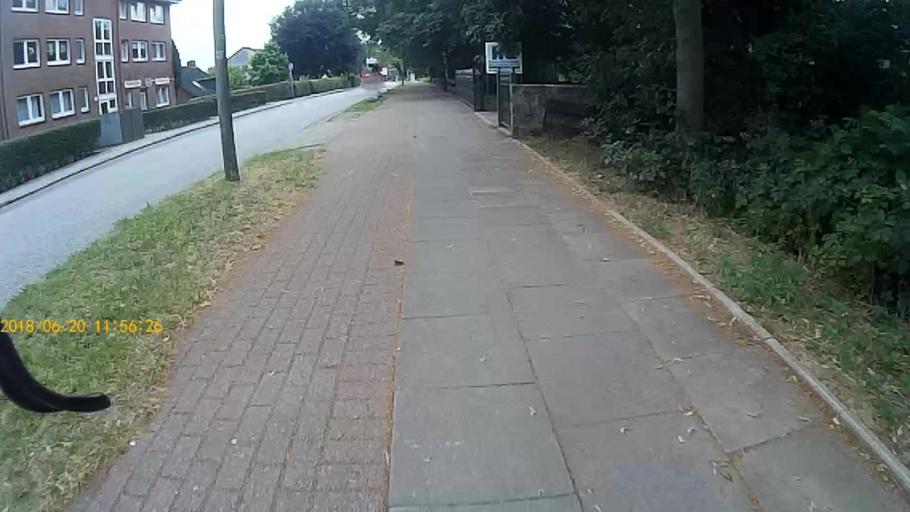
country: DE
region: Hamburg
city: Rothenburgsort
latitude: 53.5100
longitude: 10.0210
